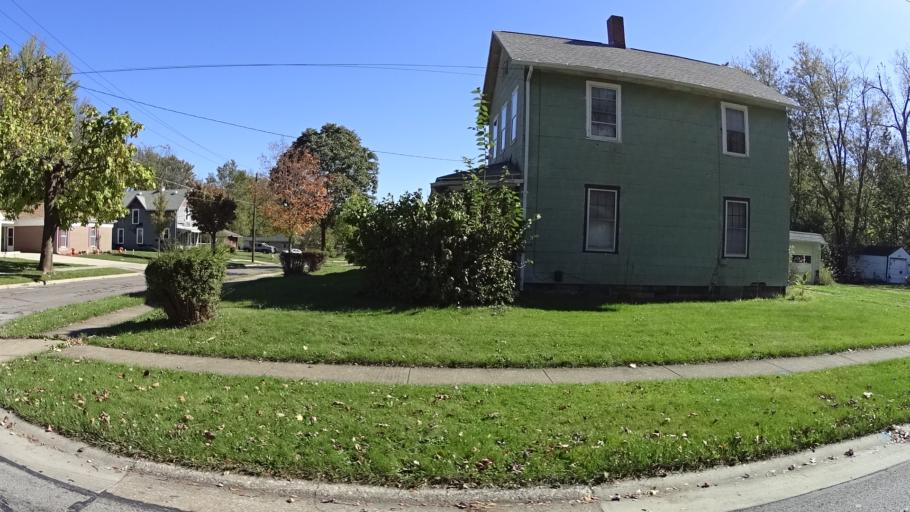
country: US
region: Ohio
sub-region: Lorain County
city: Oberlin
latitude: 41.2874
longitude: -82.2126
